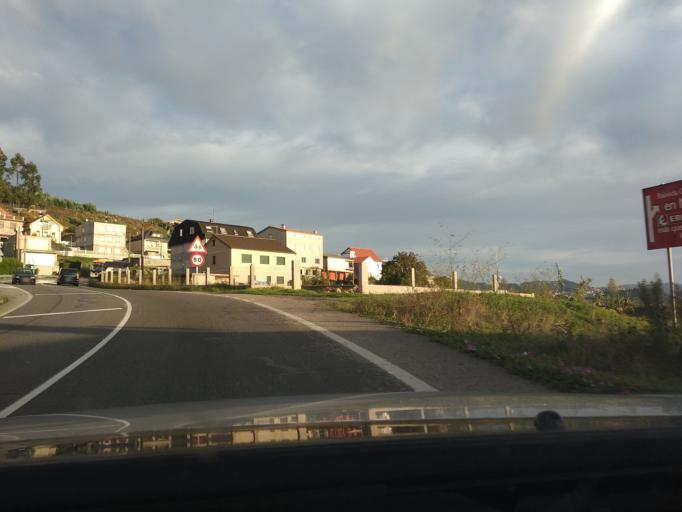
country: ES
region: Galicia
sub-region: Provincia de Pontevedra
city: Moana
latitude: 42.2819
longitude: -8.7126
